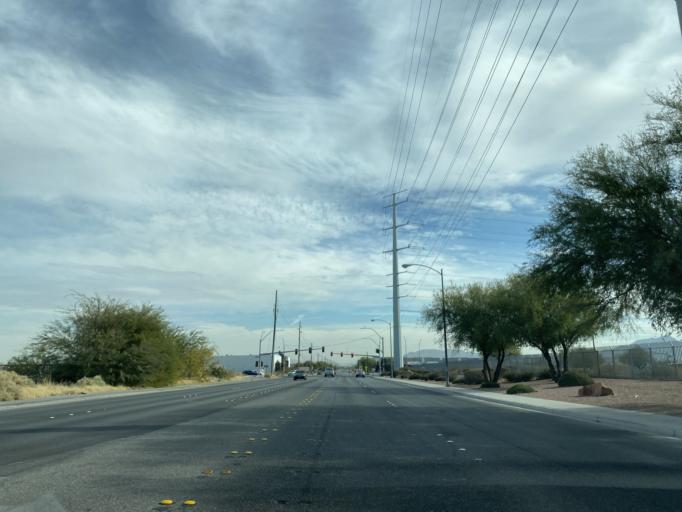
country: US
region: Nevada
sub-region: Clark County
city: North Las Vegas
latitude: 36.2469
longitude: -115.1187
